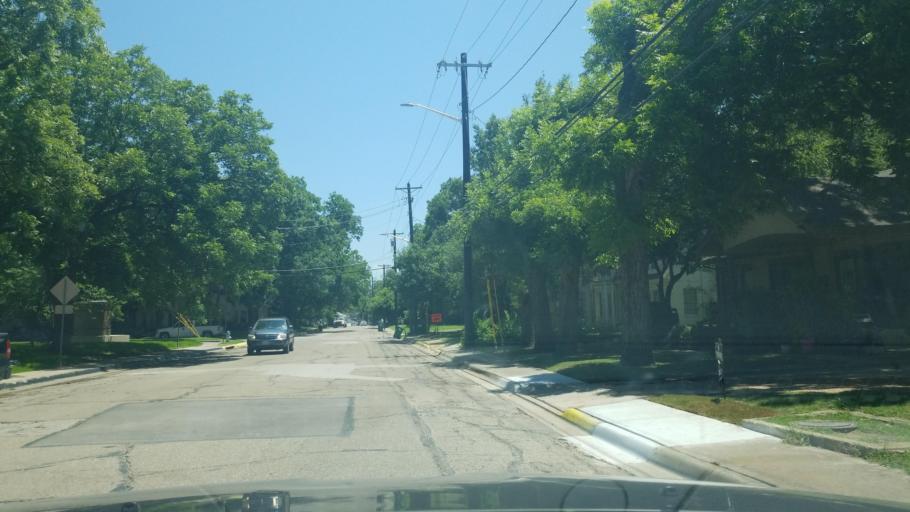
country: US
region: Texas
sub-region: Denton County
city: Denton
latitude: 33.2229
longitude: -97.1300
